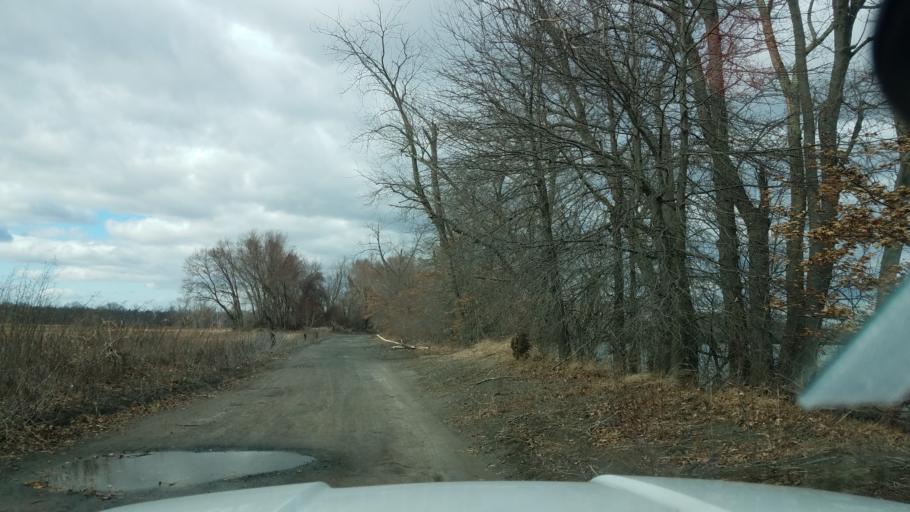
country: US
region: Connecticut
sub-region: Hartford County
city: Wethersfield
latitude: 41.6900
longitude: -72.6360
